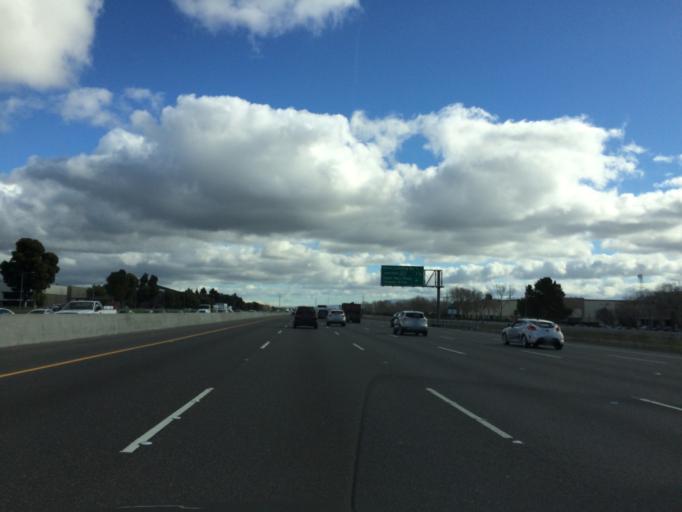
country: US
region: California
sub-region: Santa Clara County
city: Milpitas
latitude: 37.4720
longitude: -121.9306
